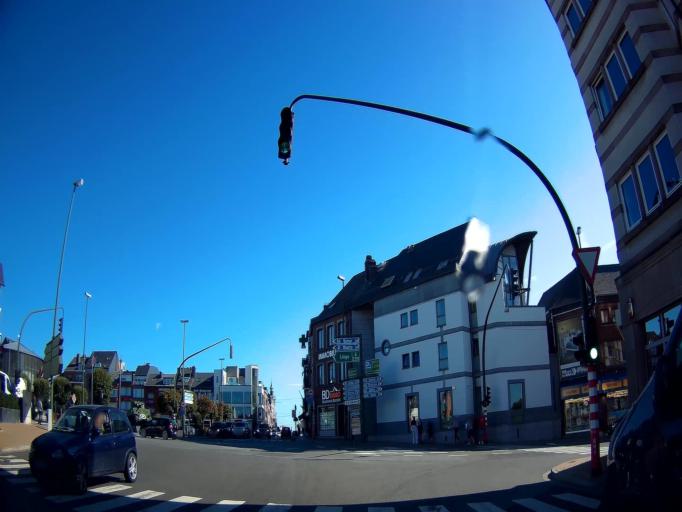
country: BE
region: Wallonia
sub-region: Province du Luxembourg
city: Bastogne
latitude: 50.0003
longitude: 5.7151
